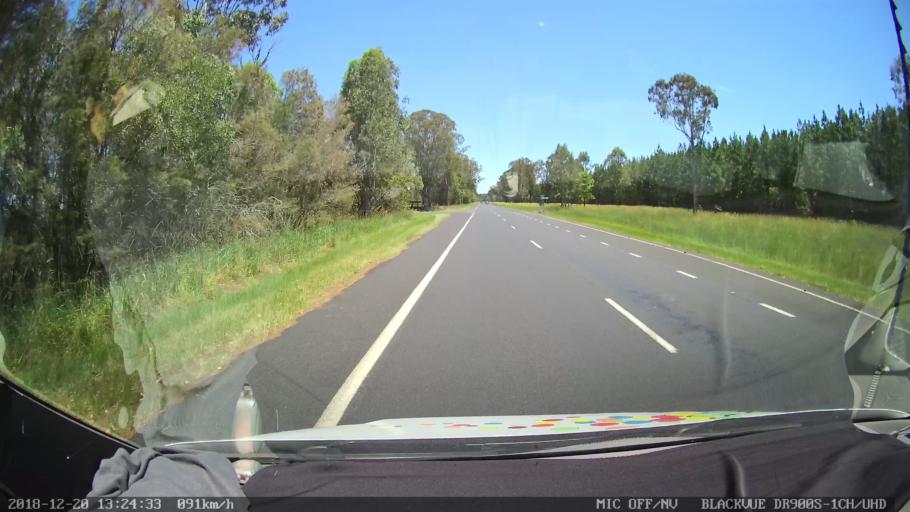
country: AU
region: New South Wales
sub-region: Richmond Valley
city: Casino
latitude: -29.1191
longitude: 152.9998
